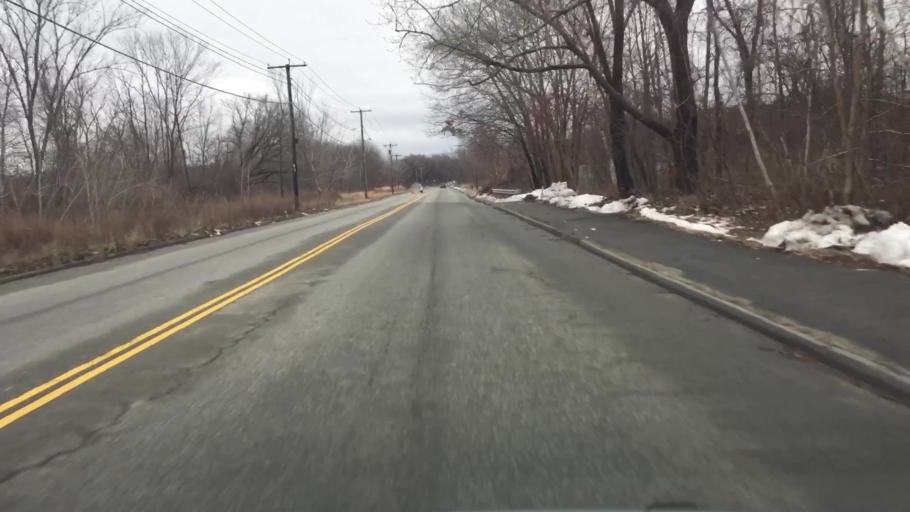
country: US
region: Massachusetts
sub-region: Worcester County
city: Hamilton
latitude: 42.3072
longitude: -71.7661
